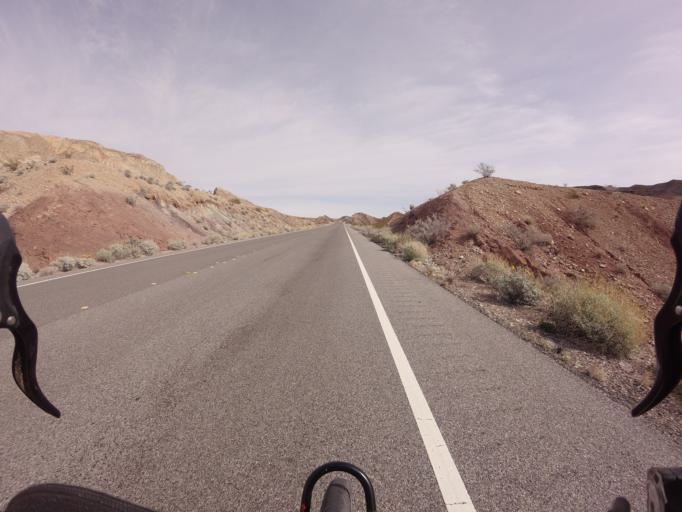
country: US
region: Nevada
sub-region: Clark County
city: Boulder City
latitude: 36.1946
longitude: -114.7129
